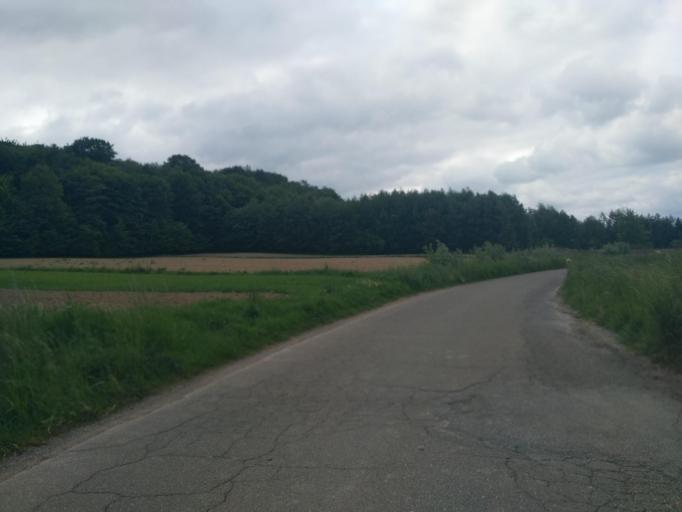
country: PL
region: Subcarpathian Voivodeship
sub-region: Powiat jasielski
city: Tarnowiec
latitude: 49.6900
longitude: 21.5839
